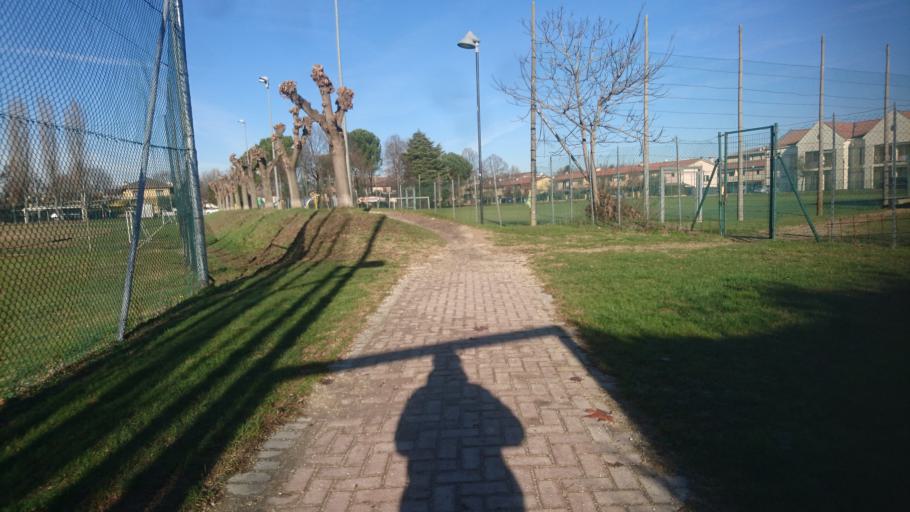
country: IT
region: Veneto
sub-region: Provincia di Padova
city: Limena
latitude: 45.4815
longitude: 11.8381
